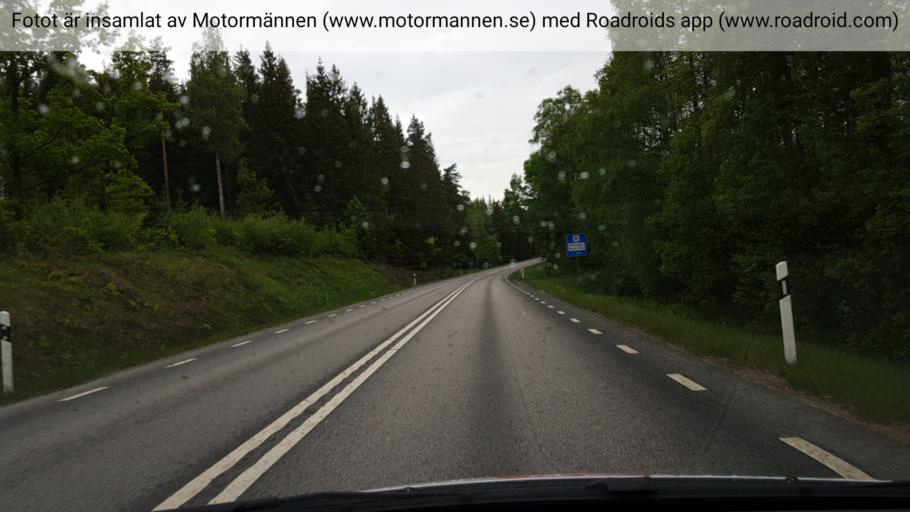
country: SE
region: Kalmar
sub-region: Hultsfreds Kommun
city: Hultsfred
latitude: 57.4931
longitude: 15.8227
